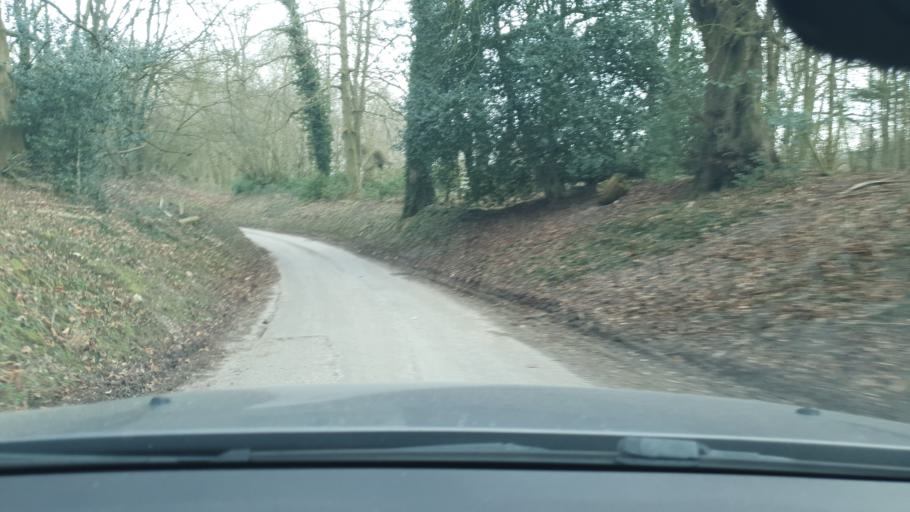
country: GB
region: England
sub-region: Wiltshire
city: Shalbourne
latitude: 51.3677
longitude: -1.5062
